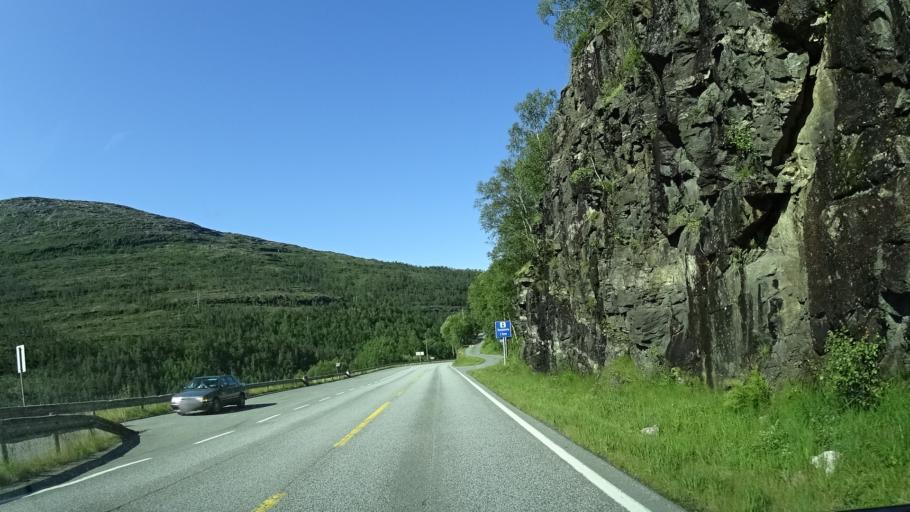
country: NO
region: Hordaland
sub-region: Samnanger
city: Tysse
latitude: 60.3818
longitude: 5.8785
